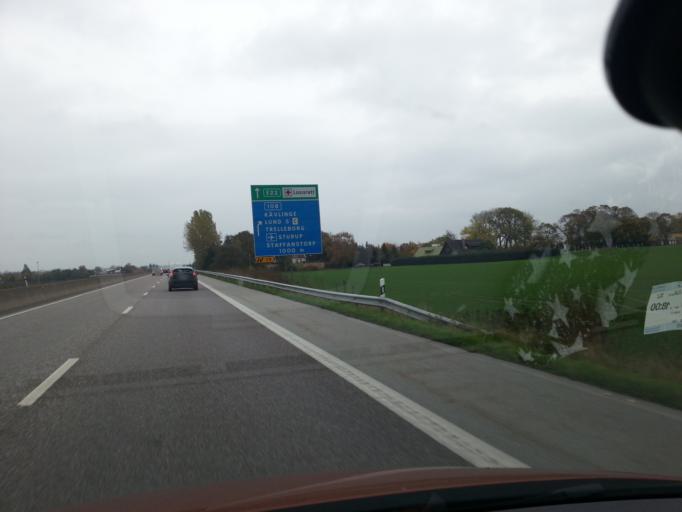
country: SE
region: Skane
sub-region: Staffanstorps Kommun
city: Hjaerup
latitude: 55.6688
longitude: 13.1654
